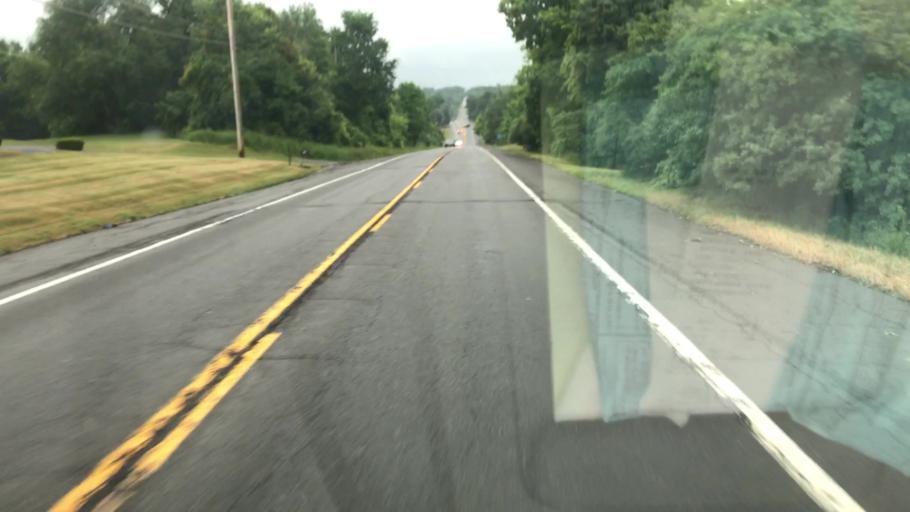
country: US
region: New York
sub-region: Onondaga County
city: Fayetteville
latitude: 43.0252
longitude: -76.0380
